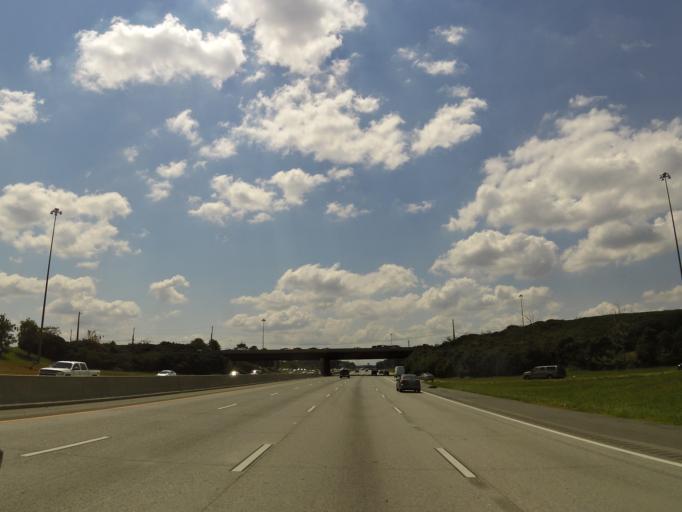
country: US
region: North Carolina
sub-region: Cabarrus County
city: Harrisburg
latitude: 35.3701
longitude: -80.7126
